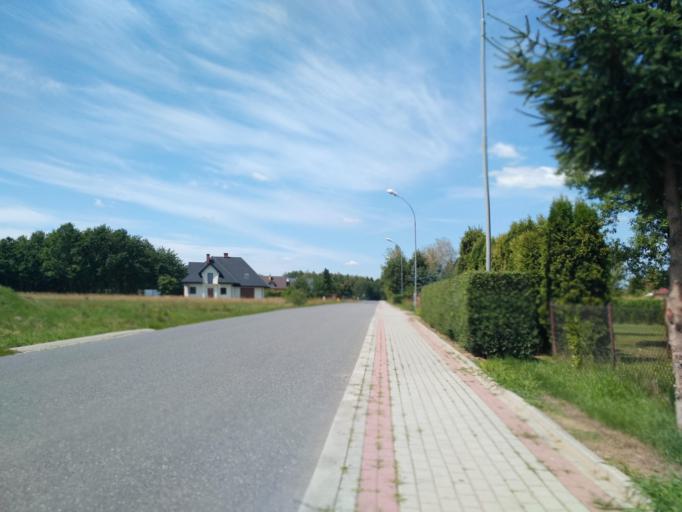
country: PL
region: Subcarpathian Voivodeship
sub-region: Powiat krosnienski
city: Kroscienko Wyzne
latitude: 49.6710
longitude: 21.8401
